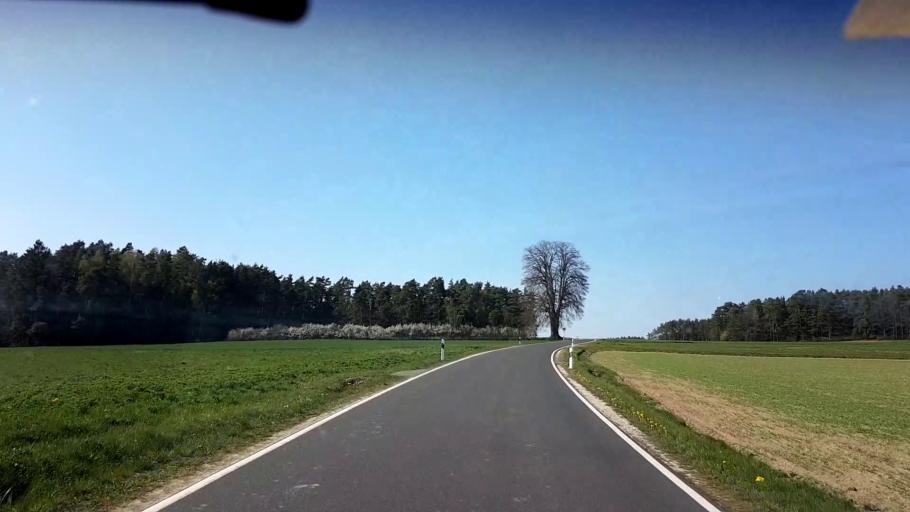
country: DE
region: Bavaria
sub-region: Upper Franconia
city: Pottenstein
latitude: 49.8007
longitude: 11.3746
